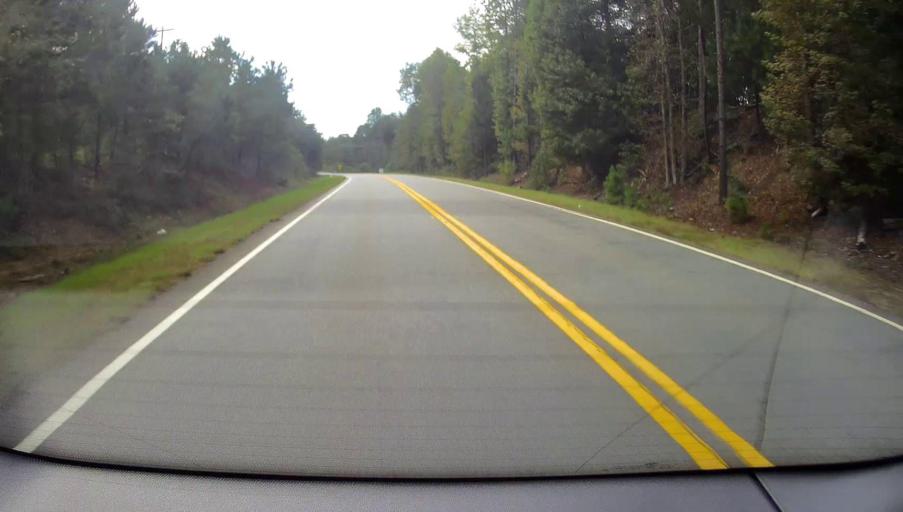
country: US
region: Georgia
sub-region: Jones County
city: Gray
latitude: 32.9834
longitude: -83.4142
